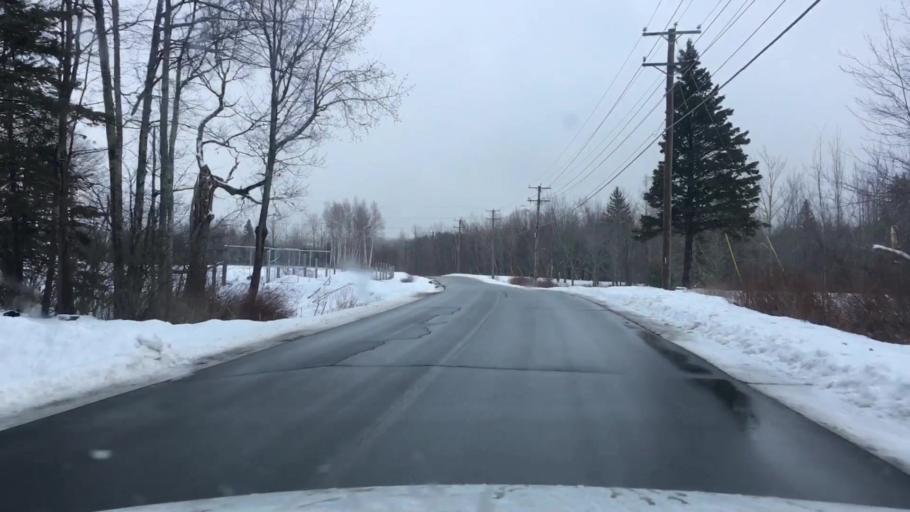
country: US
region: Maine
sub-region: Hancock County
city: Trenton
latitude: 44.4089
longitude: -68.3295
